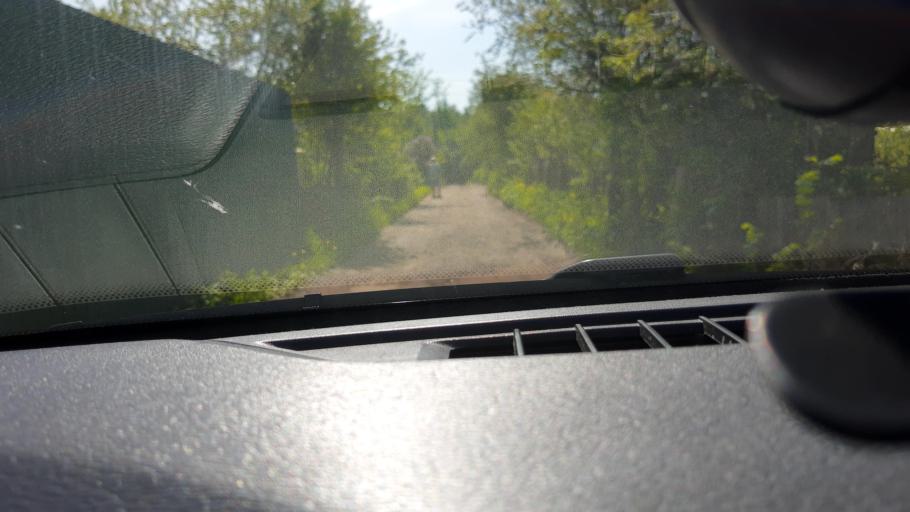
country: RU
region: Nizjnij Novgorod
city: Gorbatovka
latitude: 56.2779
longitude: 43.7874
